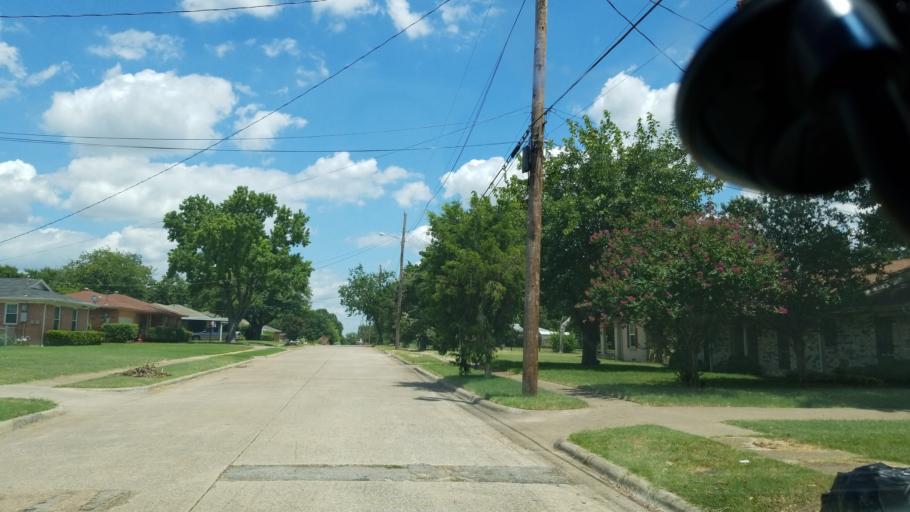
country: US
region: Texas
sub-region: Dallas County
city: Cockrell Hill
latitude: 32.6970
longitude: -96.8722
